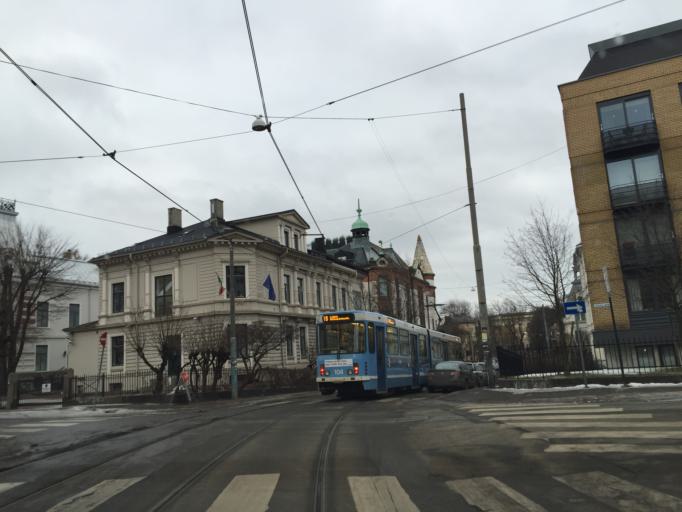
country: NO
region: Oslo
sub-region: Oslo
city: Oslo
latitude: 59.9189
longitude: 10.7212
